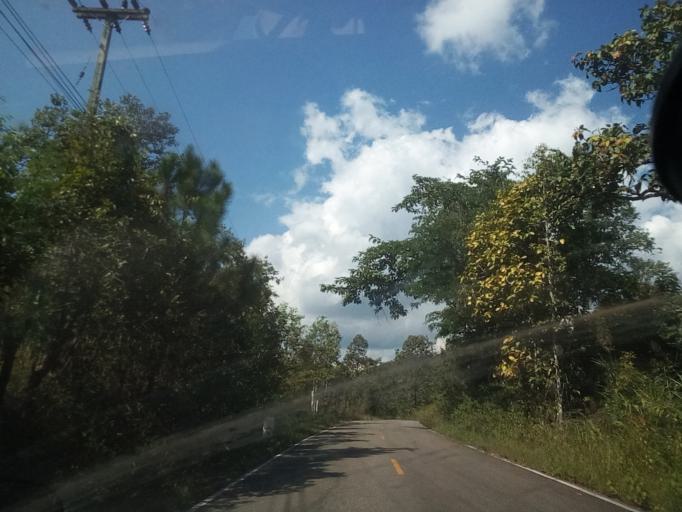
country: TH
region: Chiang Mai
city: Samoeng
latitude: 18.8634
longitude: 98.6954
